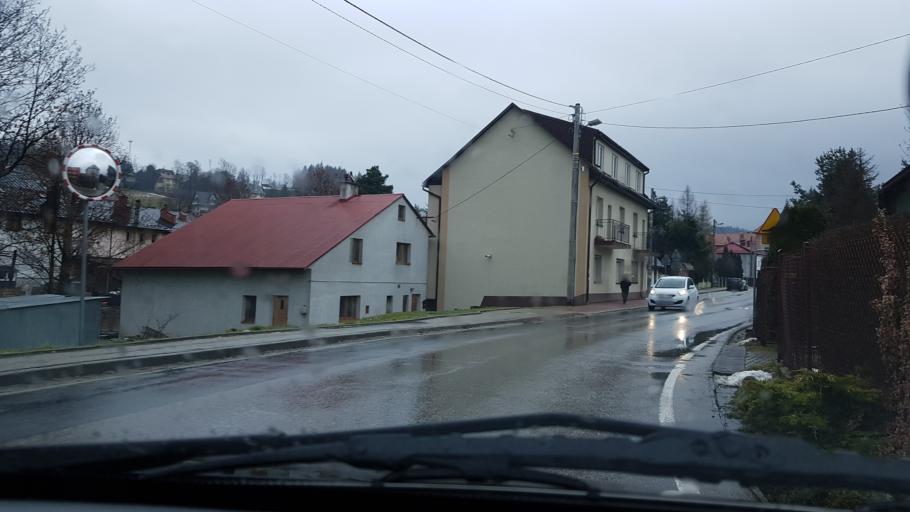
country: PL
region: Lesser Poland Voivodeship
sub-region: Powiat nowotarski
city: Raba Wyzna
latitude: 49.5668
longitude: 19.8797
